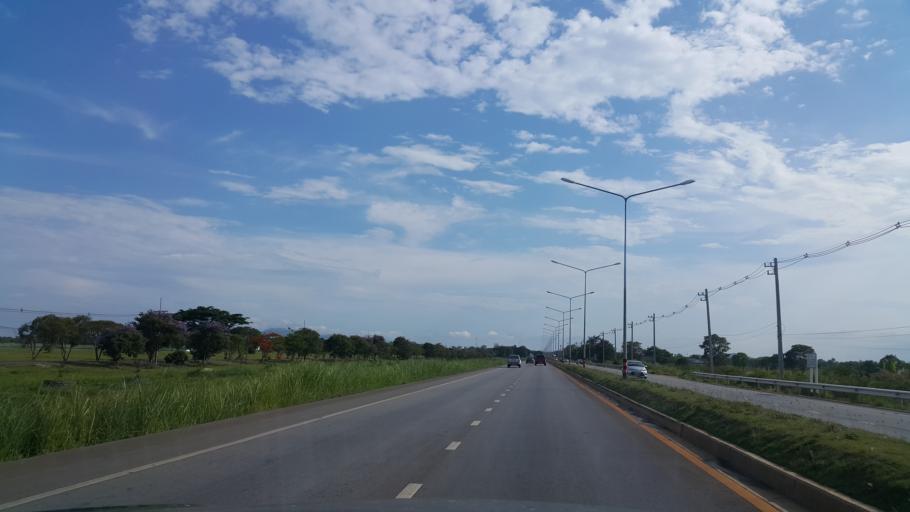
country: TH
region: Chiang Rai
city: Chiang Rai
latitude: 19.9421
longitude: 99.8695
